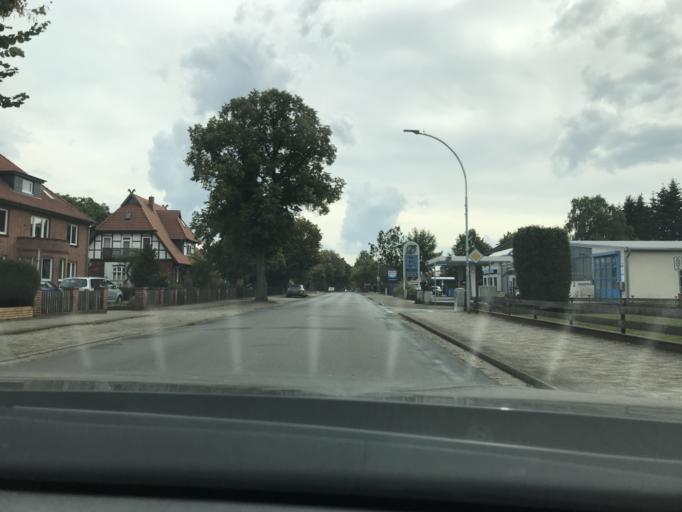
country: DE
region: Lower Saxony
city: Suderburg
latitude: 52.9028
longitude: 10.4368
